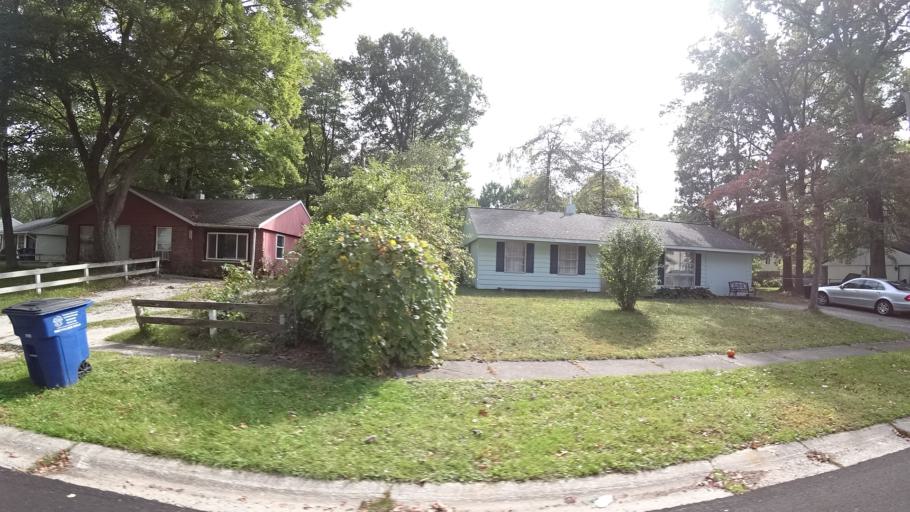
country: US
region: Indiana
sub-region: LaPorte County
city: Long Beach
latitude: 41.7178
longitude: -86.8307
